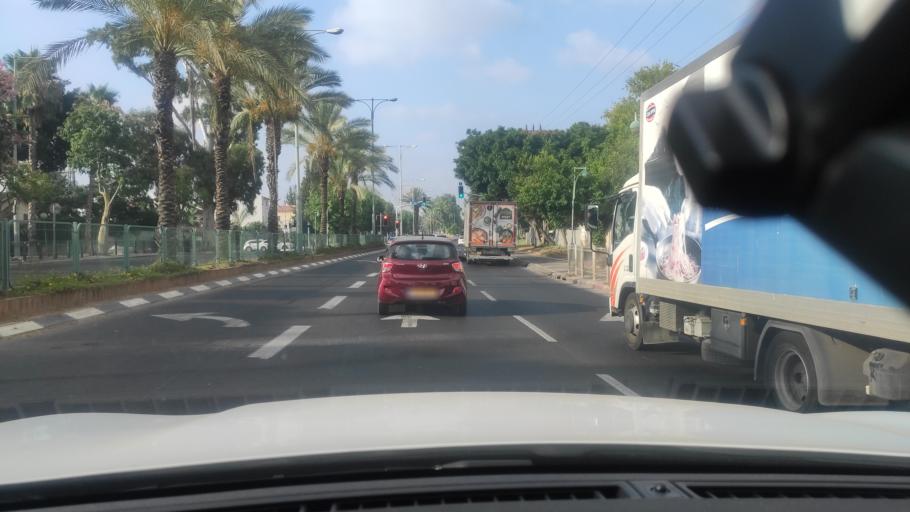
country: IL
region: Central District
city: Petah Tiqwa
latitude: 32.0917
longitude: 34.9022
